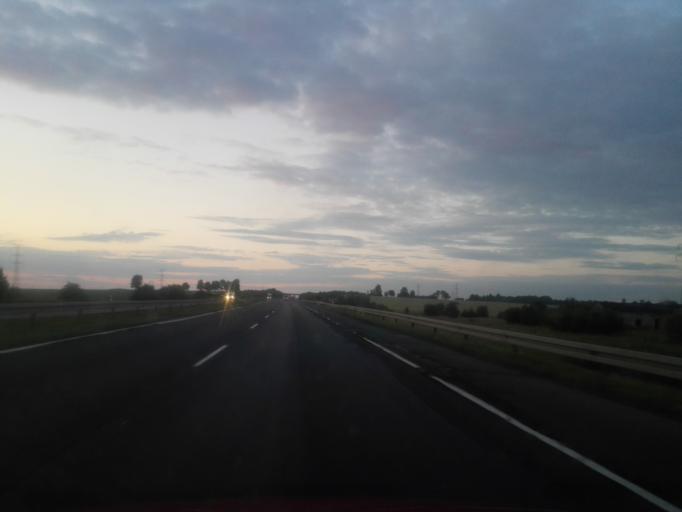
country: PL
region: Lodz Voivodeship
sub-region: Powiat radomszczanski
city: Gomunice
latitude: 51.1870
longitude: 19.4718
